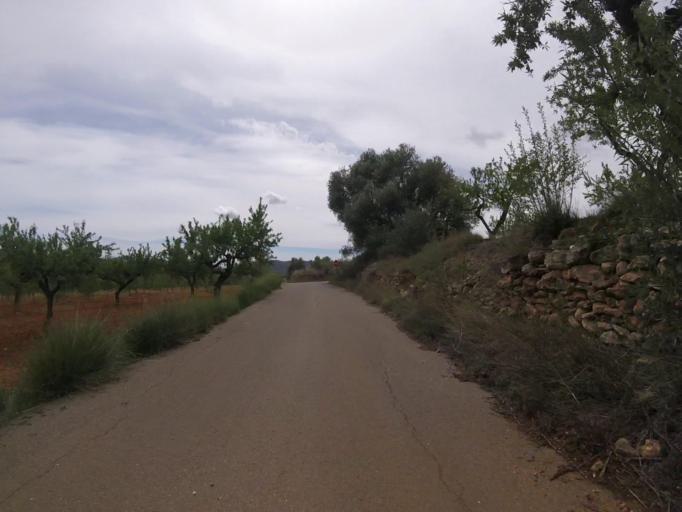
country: ES
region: Valencia
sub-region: Provincia de Castello
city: Benlloch
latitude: 40.1823
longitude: -0.0080
